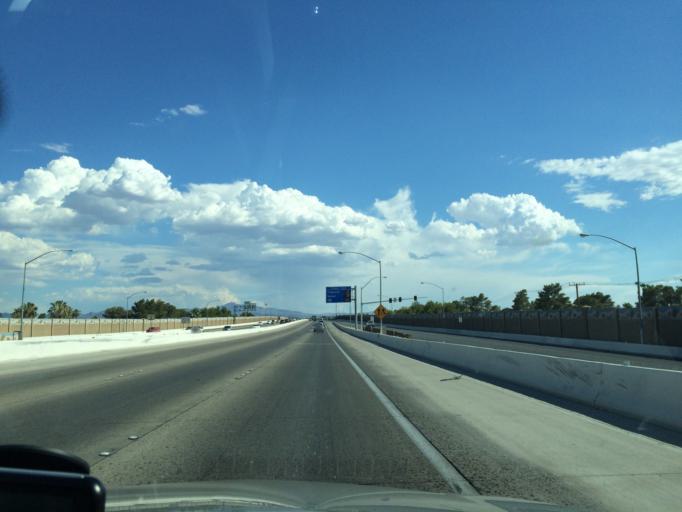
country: US
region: Nevada
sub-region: Clark County
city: Winchester
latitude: 36.1568
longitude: -115.0917
